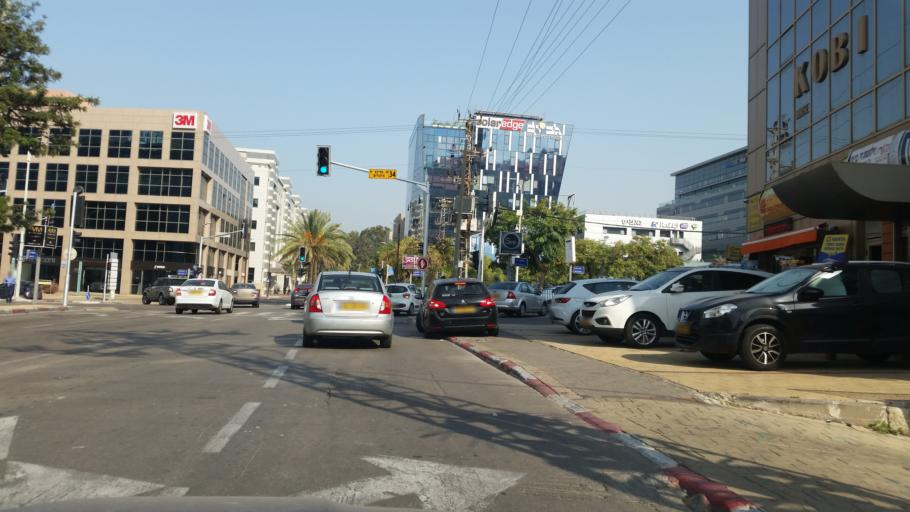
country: IL
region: Tel Aviv
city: Herzliya Pituah
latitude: 32.1654
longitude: 34.8116
